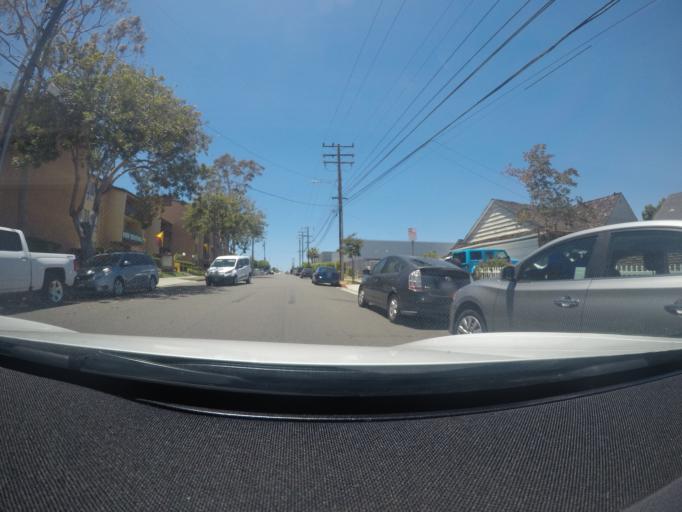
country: US
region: California
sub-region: Los Angeles County
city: Torrance
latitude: 33.8450
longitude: -118.3518
